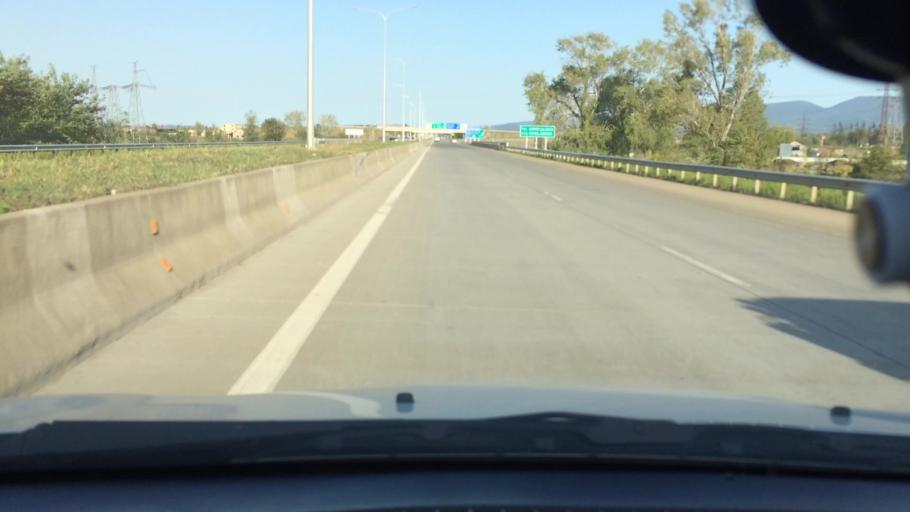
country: GE
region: Imereti
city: Zestap'oni
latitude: 42.1553
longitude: 42.9558
